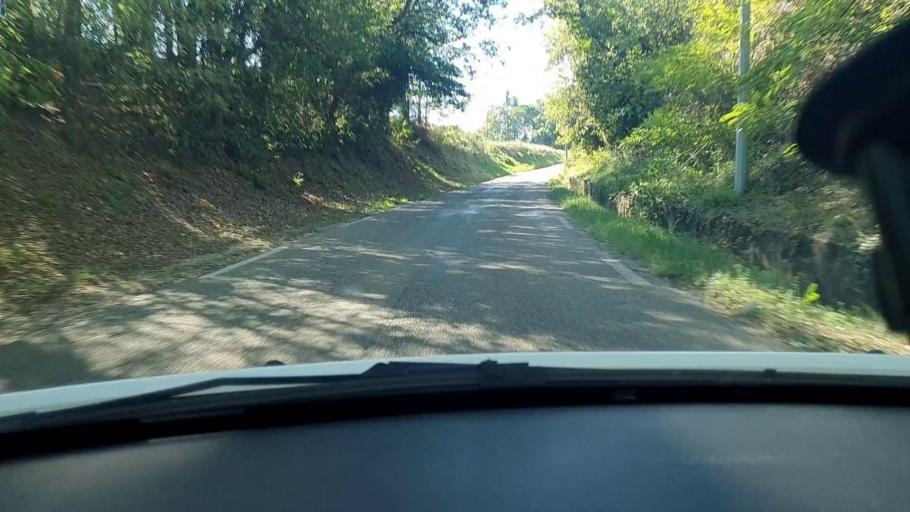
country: FR
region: Languedoc-Roussillon
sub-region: Departement du Gard
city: Saint-Julien-de-Peyrolas
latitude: 44.2785
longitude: 4.5730
